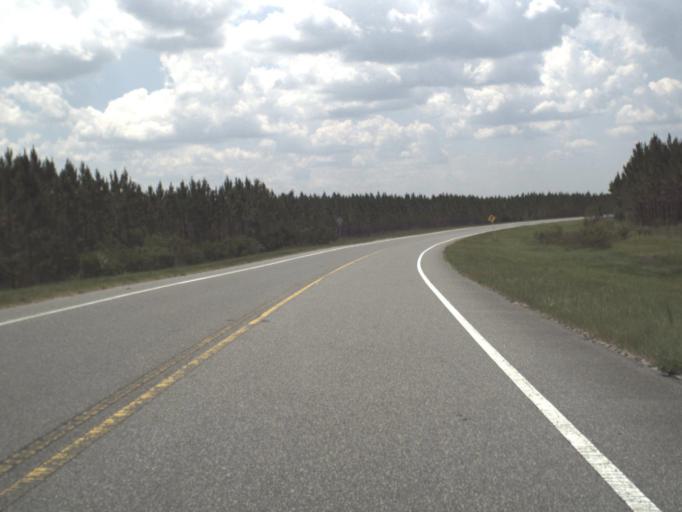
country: US
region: Florida
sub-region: Bradford County
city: Starke
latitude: 30.0002
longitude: -82.0499
